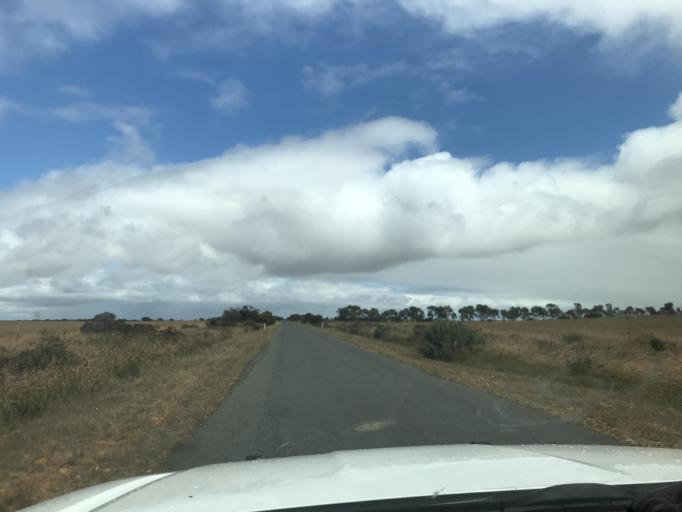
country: AU
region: South Australia
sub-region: Tatiara
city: Bordertown
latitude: -36.1381
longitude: 141.2077
